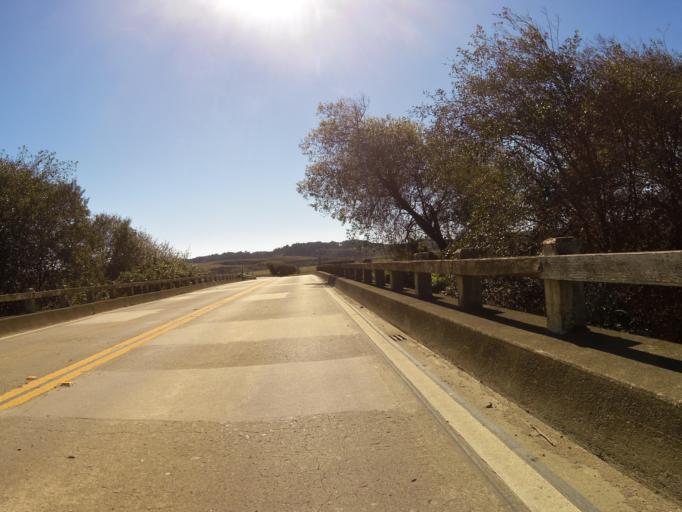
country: US
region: California
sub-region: Sonoma County
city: Sea Ranch
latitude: 38.9447
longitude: -123.7010
